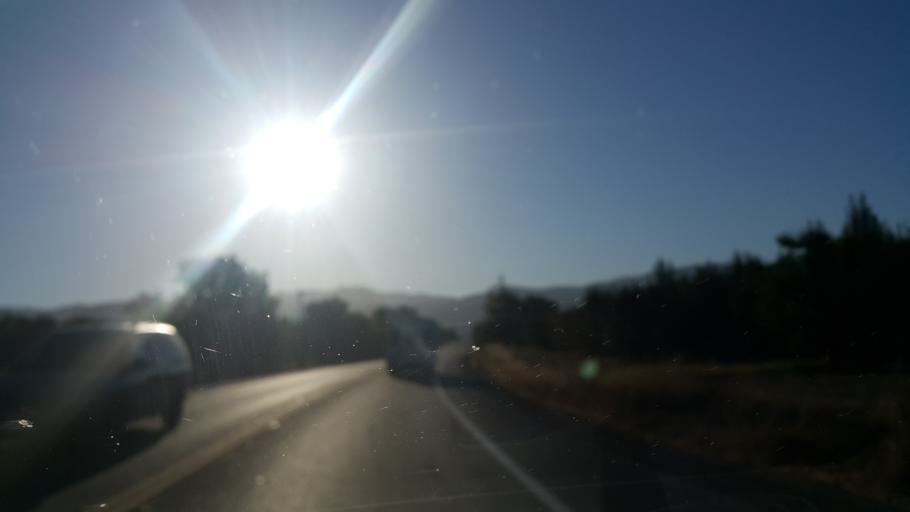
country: US
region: California
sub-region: Mendocino County
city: Ukiah
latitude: 39.1361
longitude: -123.1914
